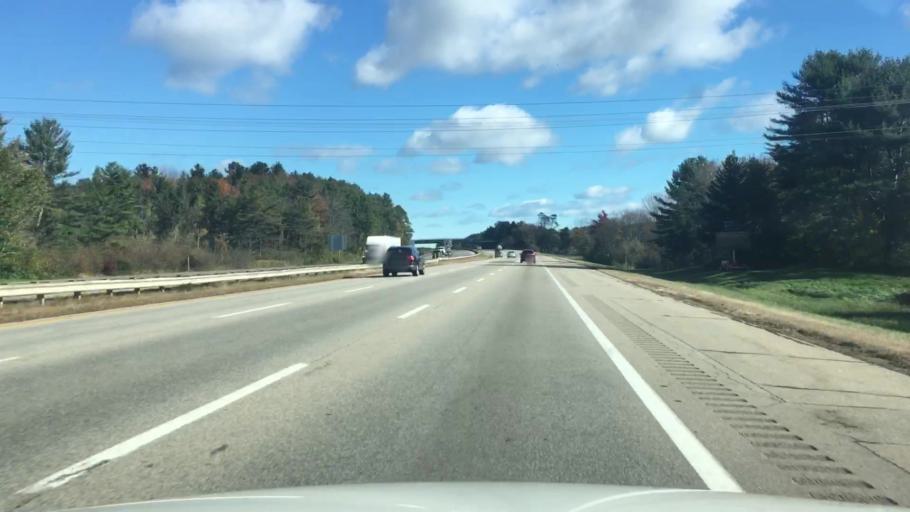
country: US
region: Maine
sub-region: York County
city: Kittery
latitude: 43.1195
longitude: -70.7282
